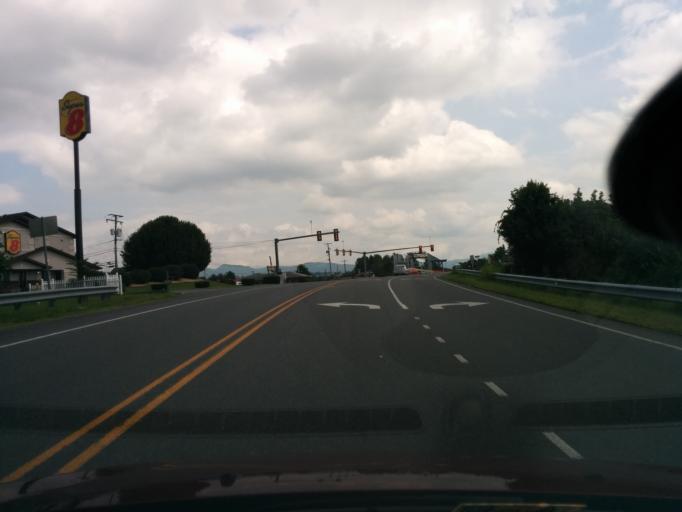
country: US
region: Virginia
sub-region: Rockbridge County
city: East Lexington
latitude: 37.8030
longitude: -79.4125
